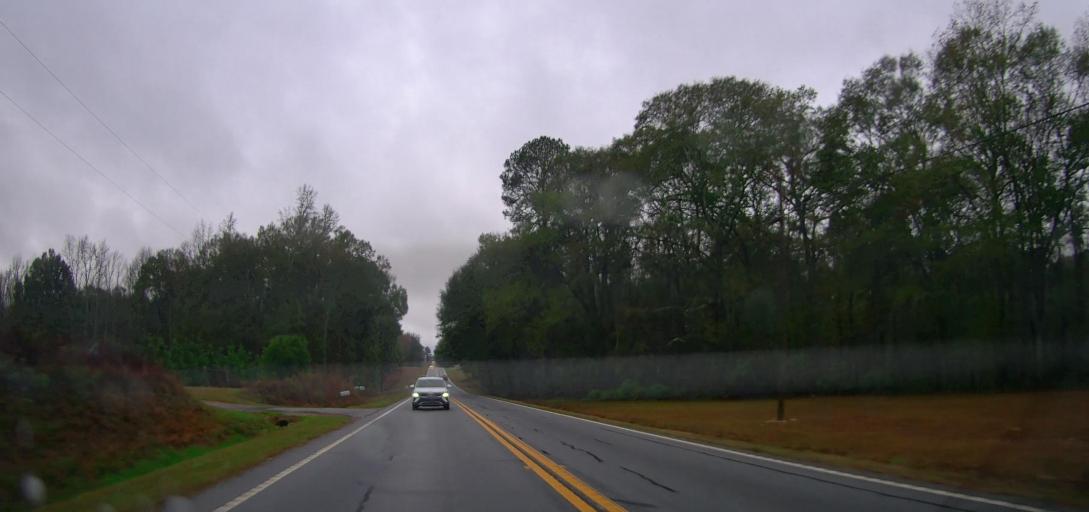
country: US
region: Georgia
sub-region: Oconee County
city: Watkinsville
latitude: 33.8350
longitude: -83.4315
